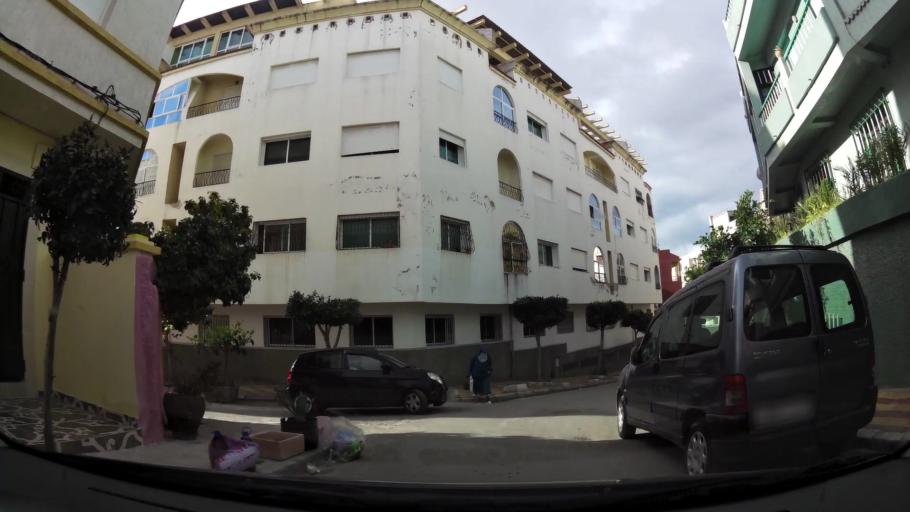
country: MA
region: Tanger-Tetouan
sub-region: Tanger-Assilah
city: Tangier
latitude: 35.7744
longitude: -5.8151
